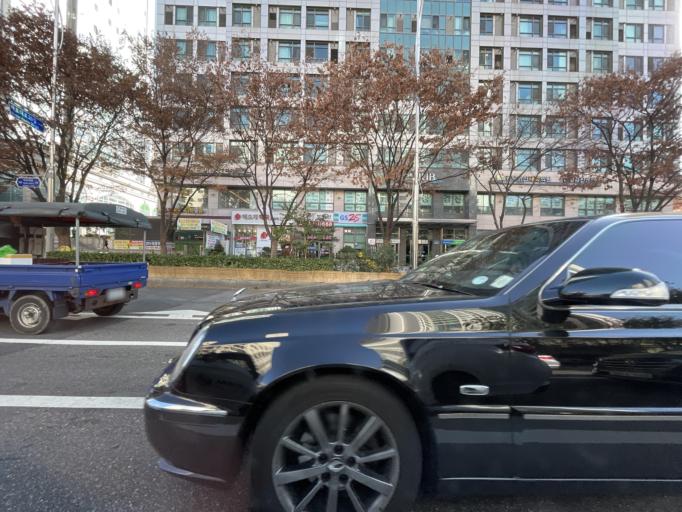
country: KR
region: Seoul
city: Seoul
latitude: 37.5522
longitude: 126.9562
